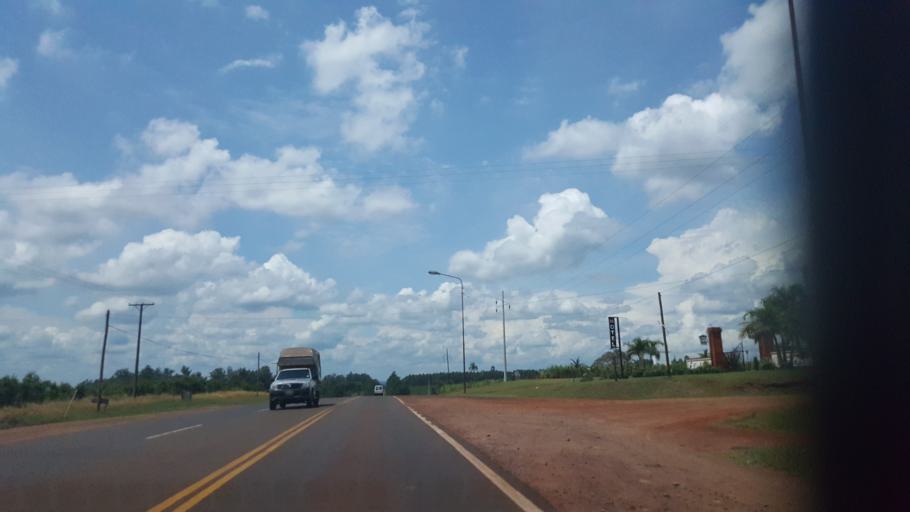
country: AR
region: Misiones
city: Puerto Rico
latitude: -26.8206
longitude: -55.0010
